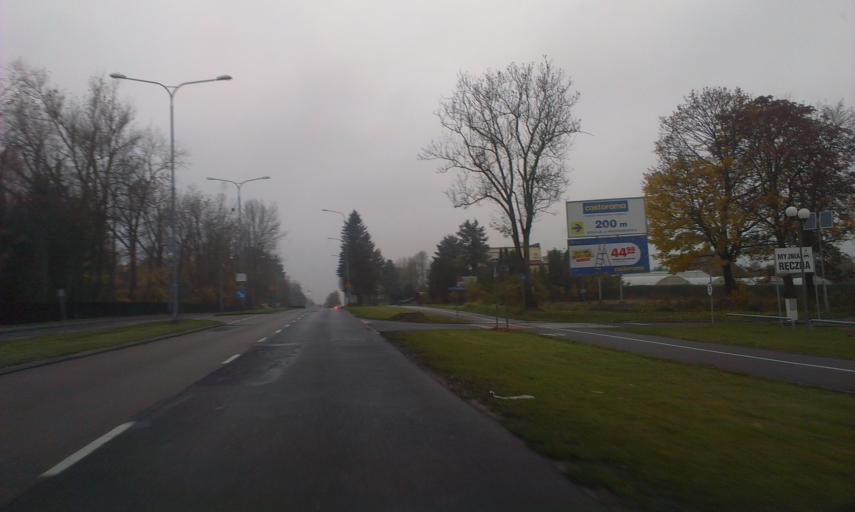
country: PL
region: West Pomeranian Voivodeship
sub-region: Koszalin
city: Koszalin
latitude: 54.1726
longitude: 16.2036
